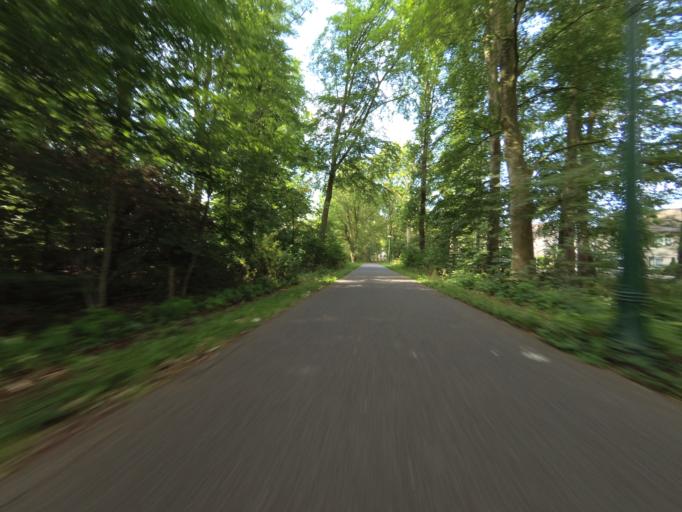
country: NL
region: Overijssel
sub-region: Gemeente Enschede
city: Enschede
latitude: 52.2391
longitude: 6.9018
